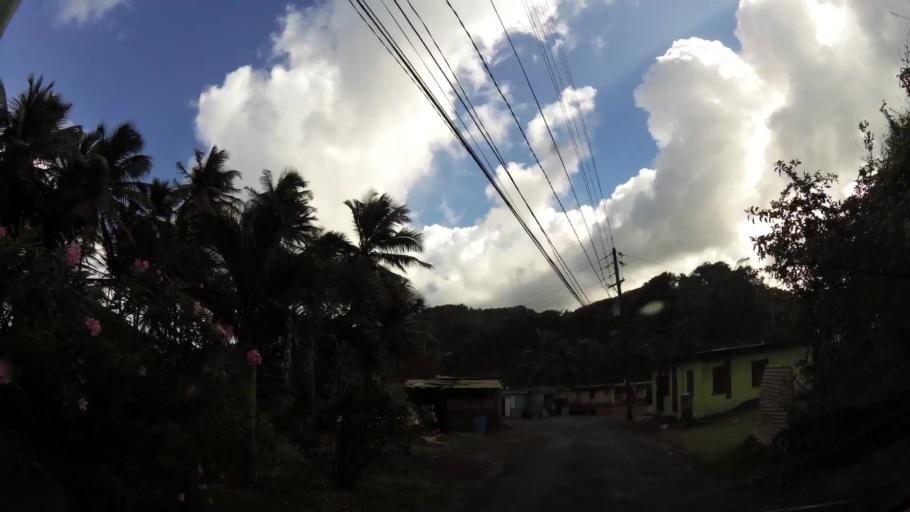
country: DM
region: Saint Andrew
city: Calibishie
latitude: 15.6008
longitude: -61.3962
